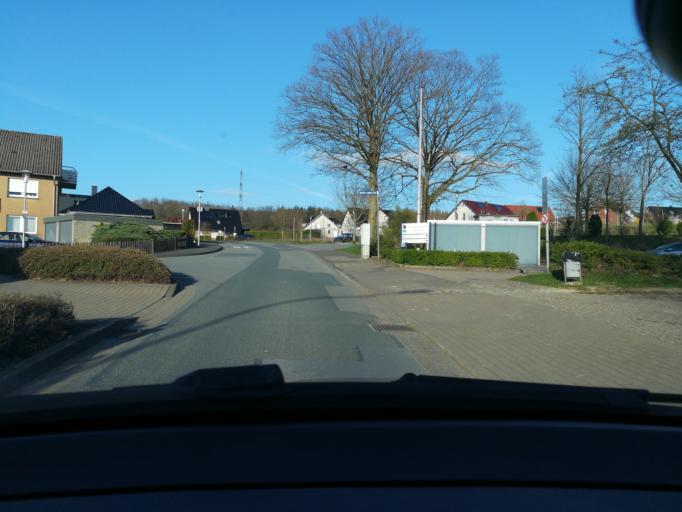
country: DE
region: North Rhine-Westphalia
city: Borgholzhausen
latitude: 52.1028
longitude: 8.3106
